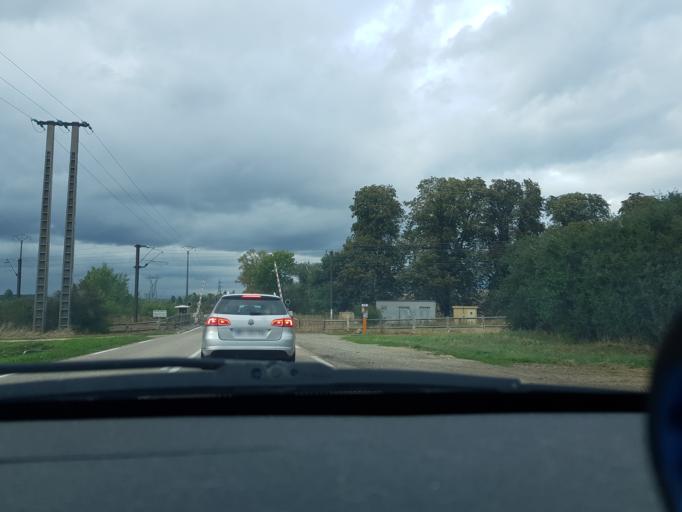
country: FR
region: Lorraine
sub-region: Departement de la Moselle
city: Morhange
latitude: 48.9542
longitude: 6.6113
